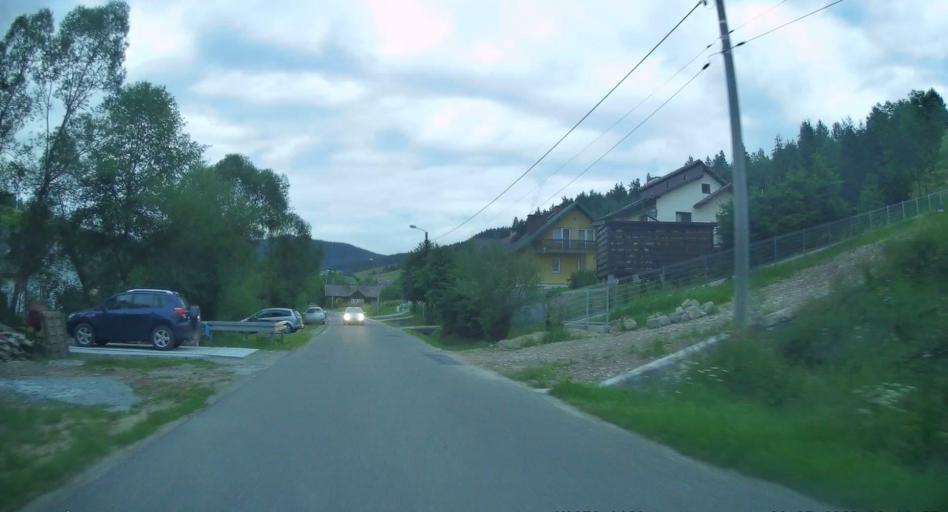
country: PL
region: Lesser Poland Voivodeship
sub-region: Powiat nowosadecki
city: Muszyna
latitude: 49.3788
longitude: 20.9235
